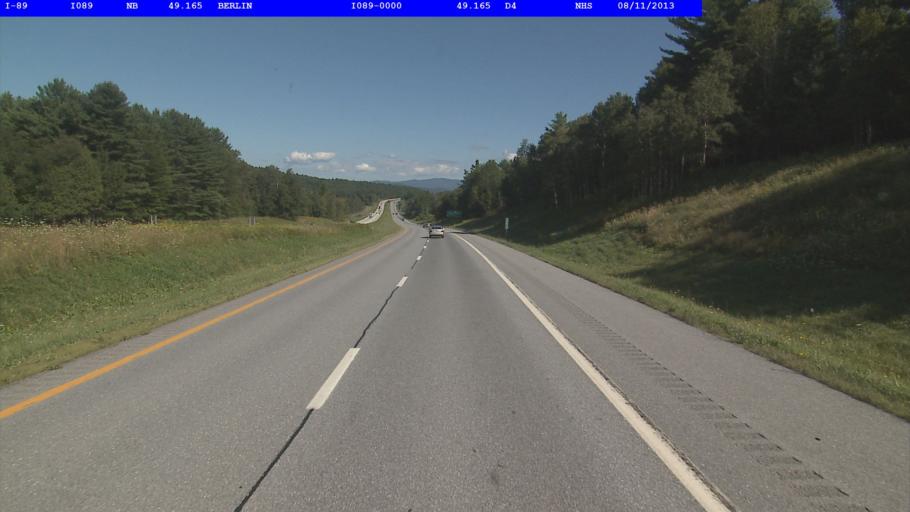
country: US
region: Vermont
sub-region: Washington County
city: Montpelier
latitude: 44.2000
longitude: -72.5773
